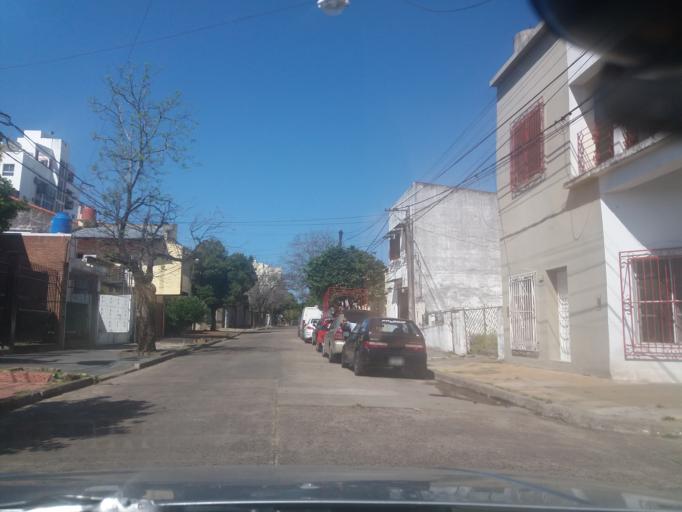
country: AR
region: Corrientes
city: Corrientes
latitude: -27.4683
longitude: -58.8495
